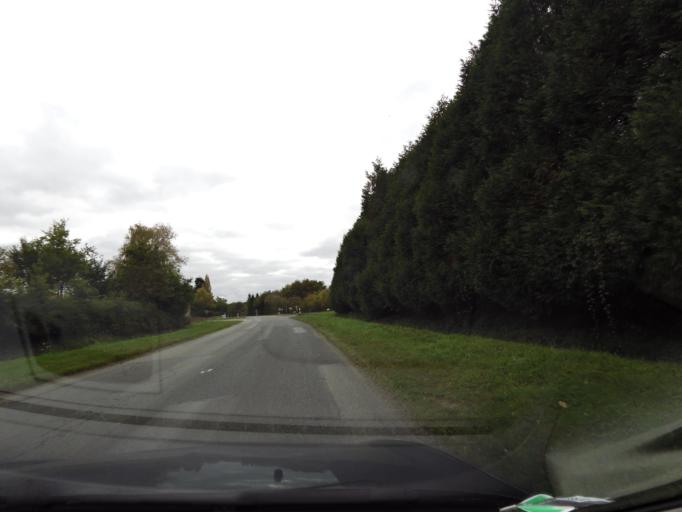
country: FR
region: Brittany
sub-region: Departement d'Ille-et-Vilaine
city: Chantepie
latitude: 48.0782
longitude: -1.6055
